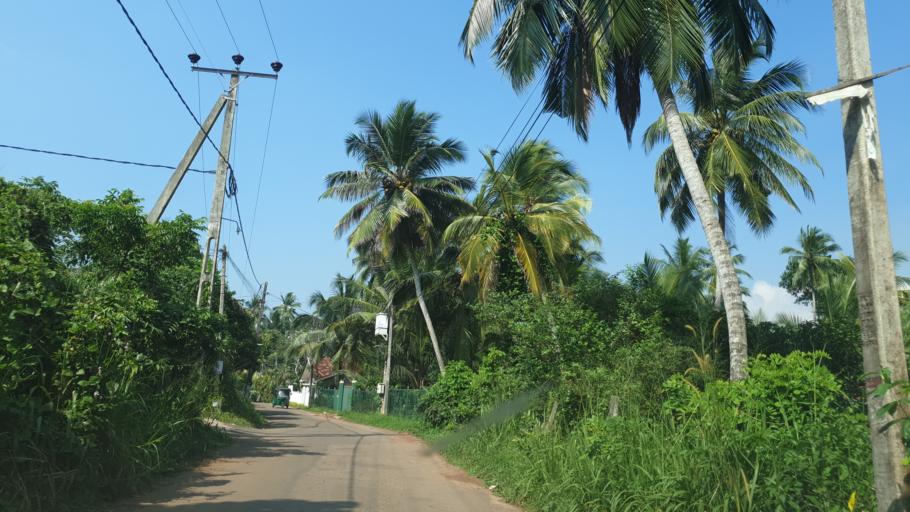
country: LK
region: Western
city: Moratuwa
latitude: 6.7623
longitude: 79.9244
